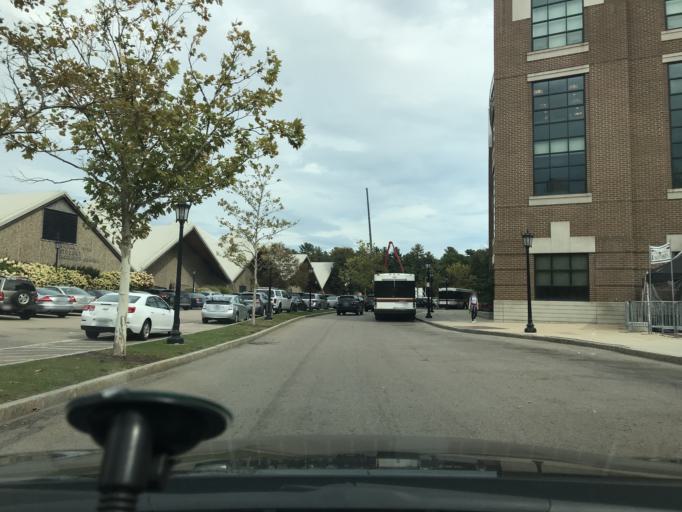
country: US
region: Massachusetts
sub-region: Middlesex County
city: Watertown
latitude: 42.3360
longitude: -71.1675
